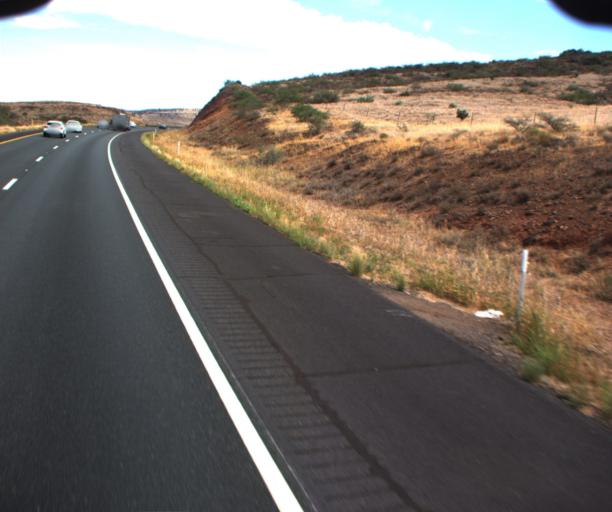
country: US
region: Arizona
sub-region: Yavapai County
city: Cordes Lakes
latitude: 34.4582
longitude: -112.0303
